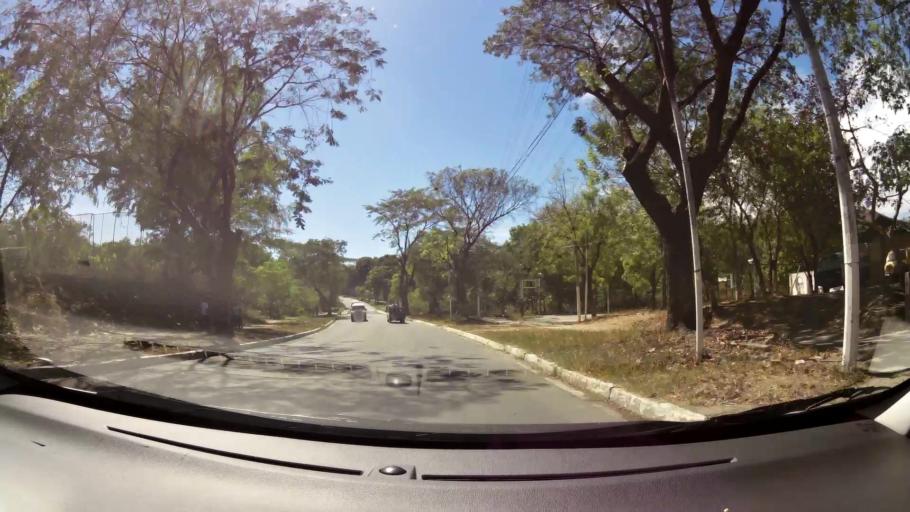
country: SV
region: San Salvador
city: Apopa
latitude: 13.8130
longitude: -89.1787
